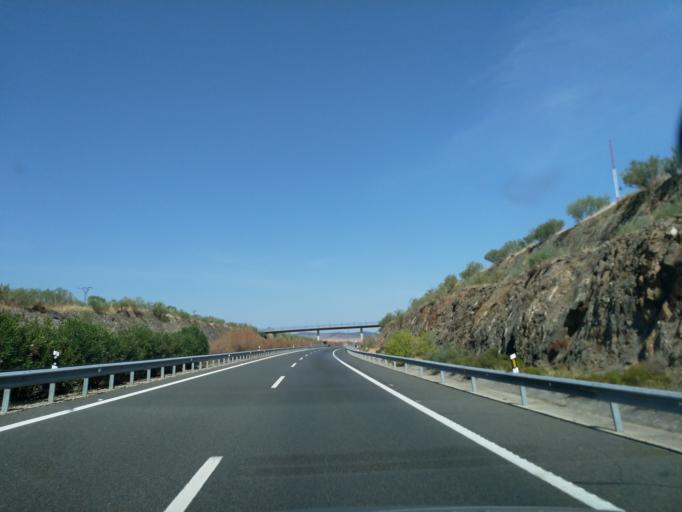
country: ES
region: Extremadura
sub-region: Provincia de Caceres
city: Aldea del Cano
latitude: 39.3436
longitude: -6.3417
